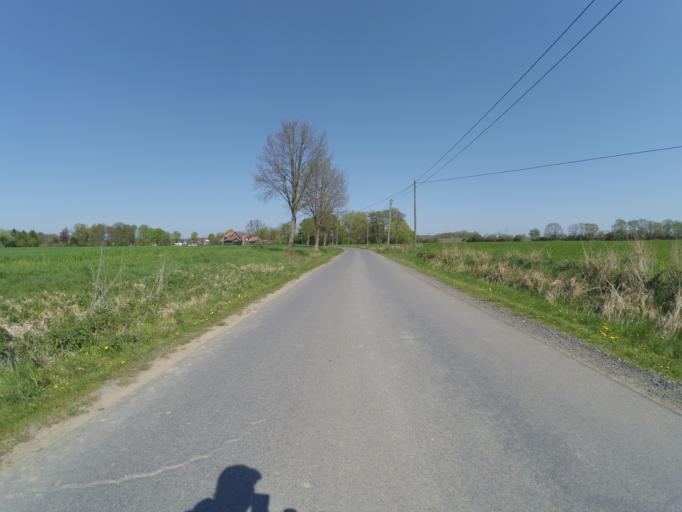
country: DE
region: North Rhine-Westphalia
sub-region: Regierungsbezirk Munster
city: Ascheberg
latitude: 51.8097
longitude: 7.5945
